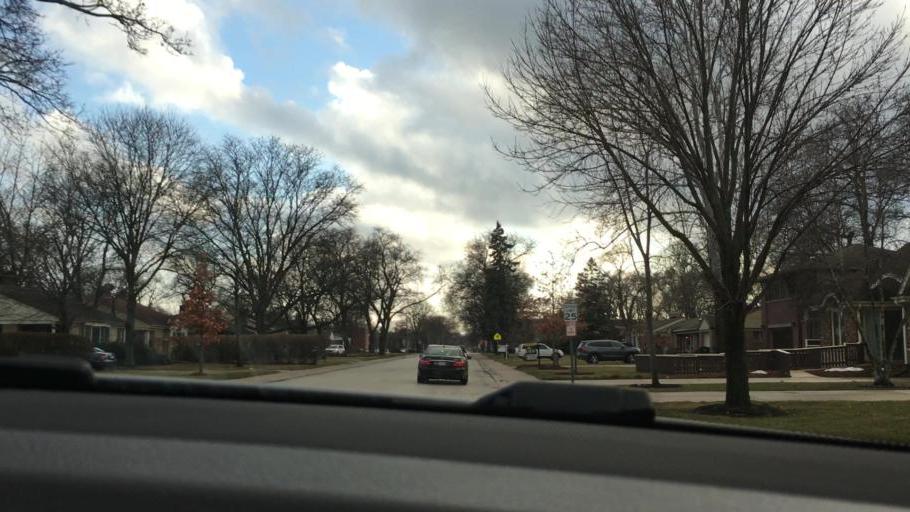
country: US
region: Illinois
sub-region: Cook County
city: Arlington Heights
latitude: 42.0864
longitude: -87.9709
